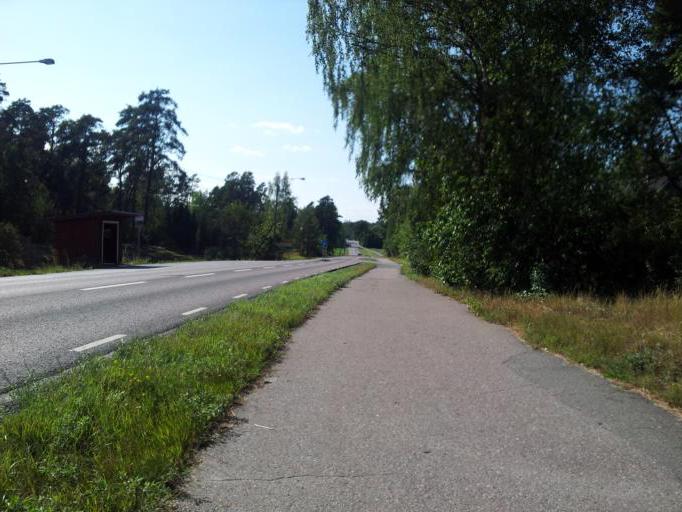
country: SE
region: Stockholm
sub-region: Norrtalje Kommun
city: Nykvarn
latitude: 59.8733
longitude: 18.0558
